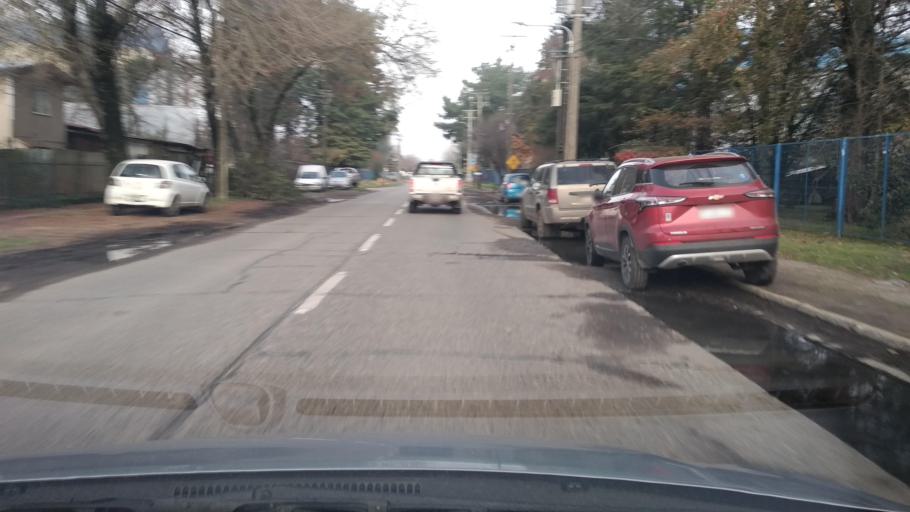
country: CL
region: Los Rios
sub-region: Provincia de Valdivia
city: Valdivia
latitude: -39.8059
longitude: -73.2374
